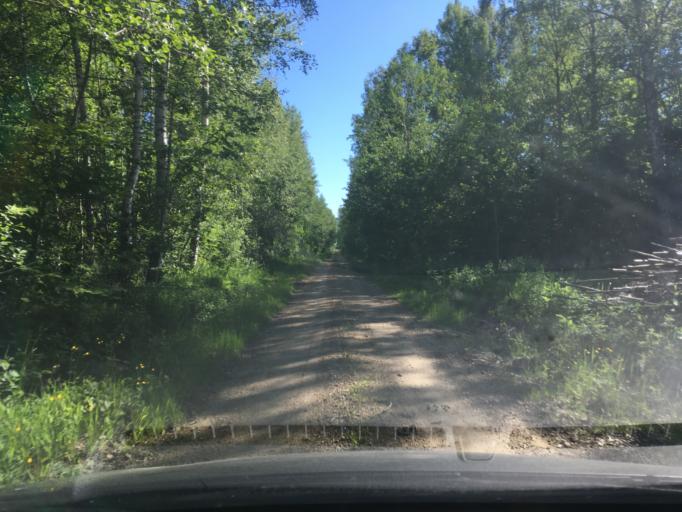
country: EE
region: Laeaene
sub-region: Lihula vald
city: Lihula
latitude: 58.6205
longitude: 23.7024
